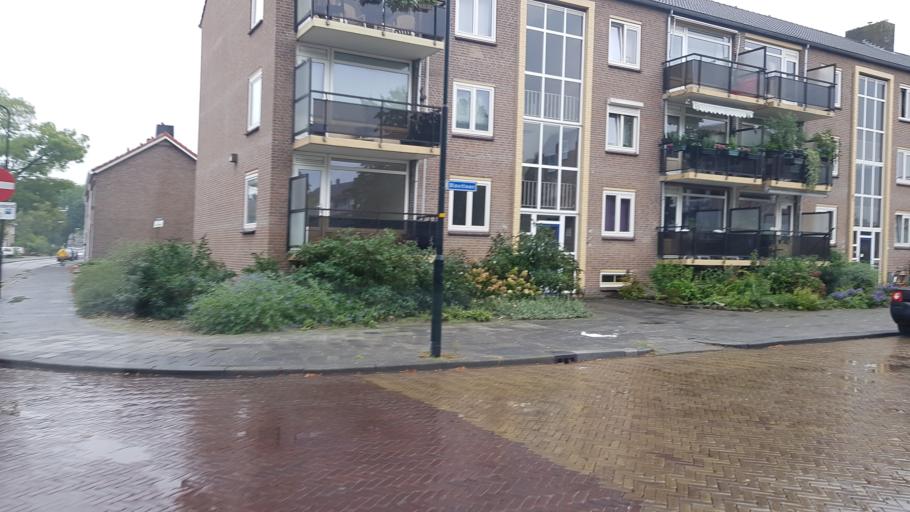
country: NL
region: Gelderland
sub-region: Gemeente Apeldoorn
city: Apeldoorn
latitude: 52.1903
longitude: 5.9671
